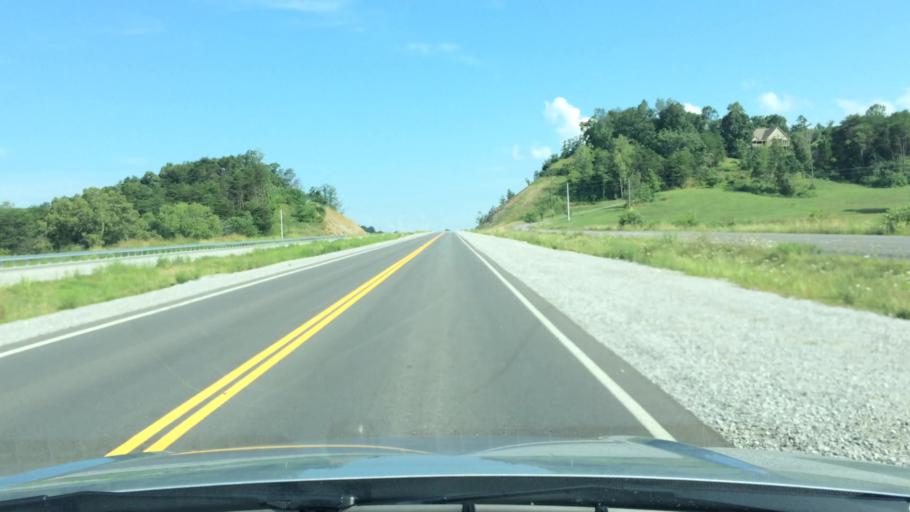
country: US
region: Tennessee
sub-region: Jefferson County
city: White Pine
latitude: 36.1328
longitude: -83.3371
